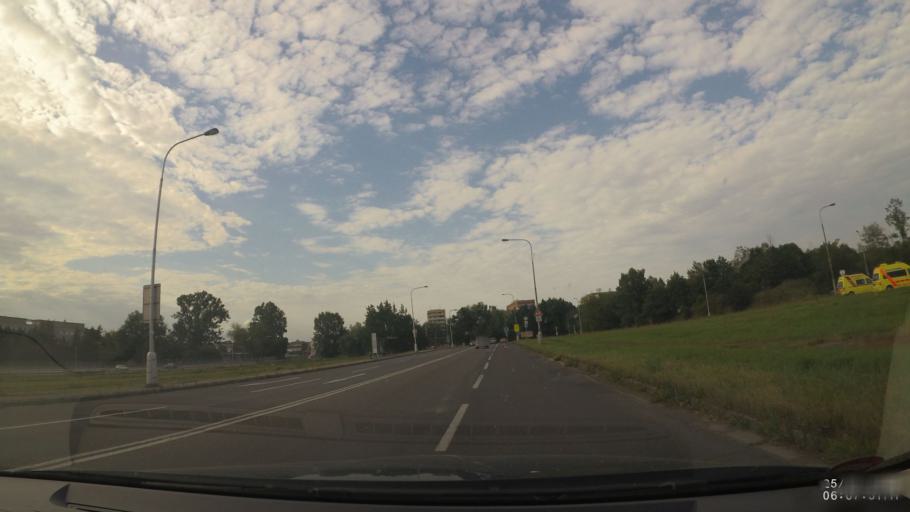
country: CZ
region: Kralovehradecky
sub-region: Okres Hradec Kralove
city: Hradec Kralove
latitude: 50.1989
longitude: 15.8325
